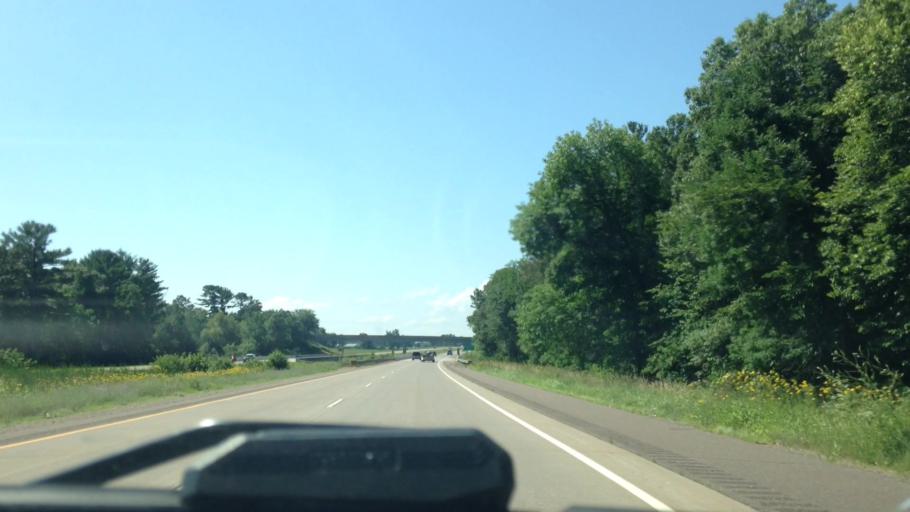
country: US
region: Wisconsin
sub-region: Barron County
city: Cameron
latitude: 45.4482
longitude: -91.7599
